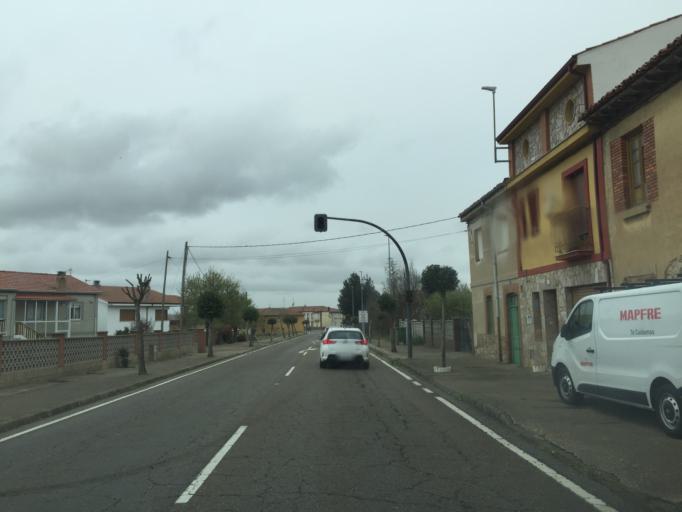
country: ES
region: Castille and Leon
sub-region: Provincia de Leon
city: Sariegos
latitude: 42.6707
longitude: -5.6354
